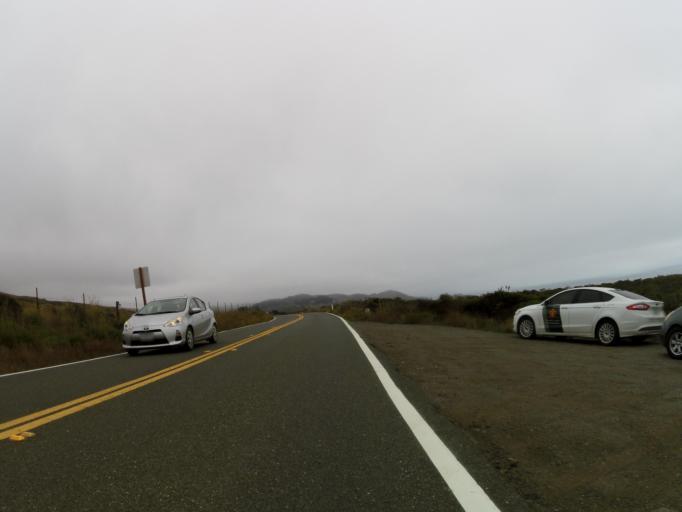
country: US
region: California
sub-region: Sonoma County
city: Monte Rio
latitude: 38.4582
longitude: -123.1417
